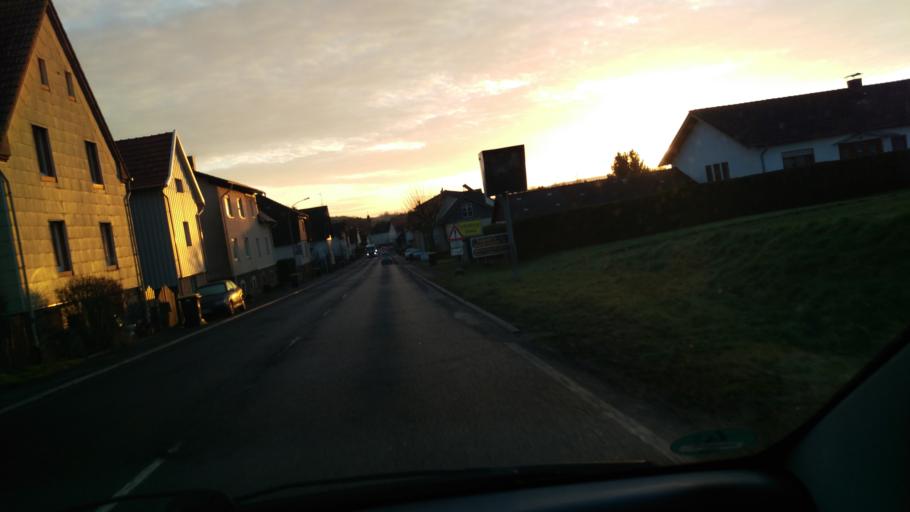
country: DE
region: Hesse
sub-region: Regierungsbezirk Giessen
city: Alsfeld
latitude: 50.7600
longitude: 9.2249
